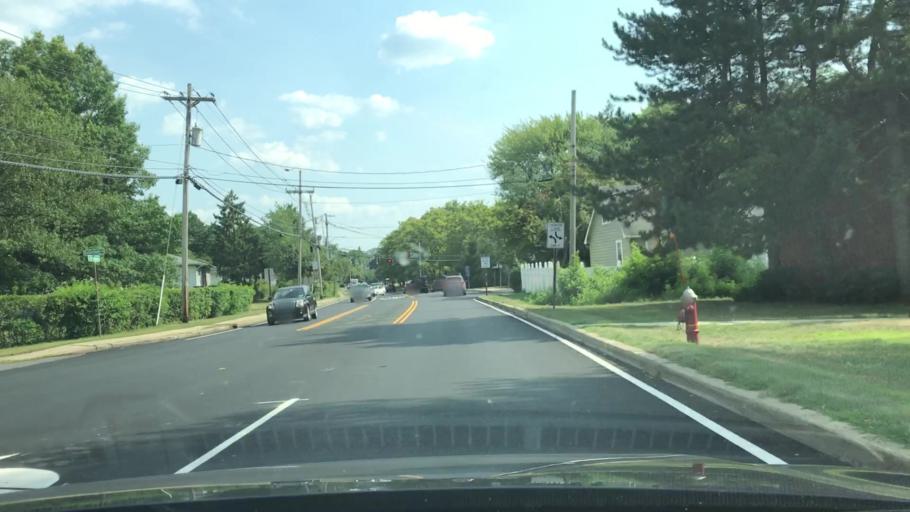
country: US
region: New York
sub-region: Rockland County
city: Bardonia
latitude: 41.1136
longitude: -74.0107
